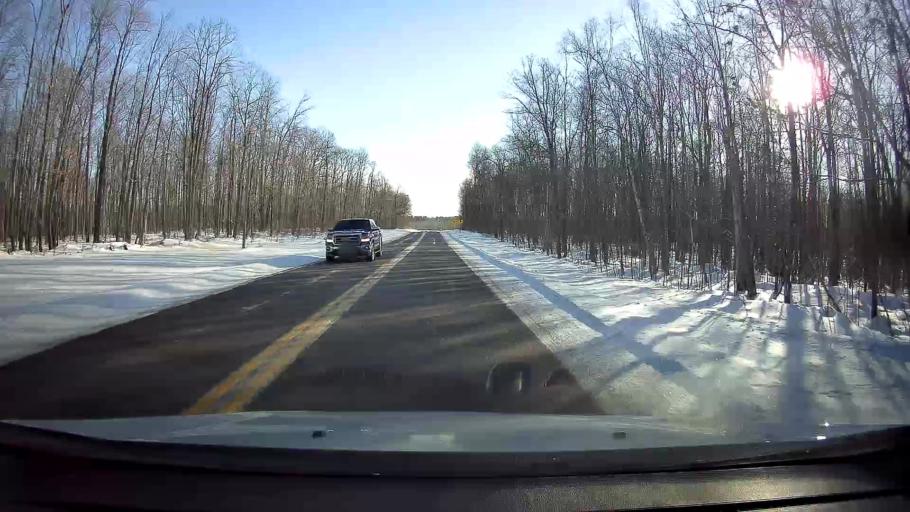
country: US
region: Wisconsin
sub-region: Sawyer County
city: Little Round Lake
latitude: 46.1144
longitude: -91.3268
